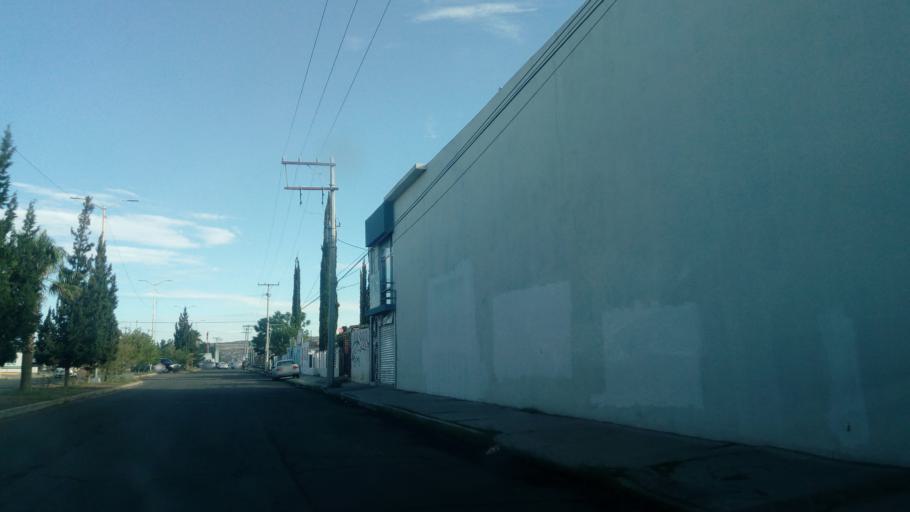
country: MX
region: Durango
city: Victoria de Durango
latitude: 24.0562
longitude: -104.6104
